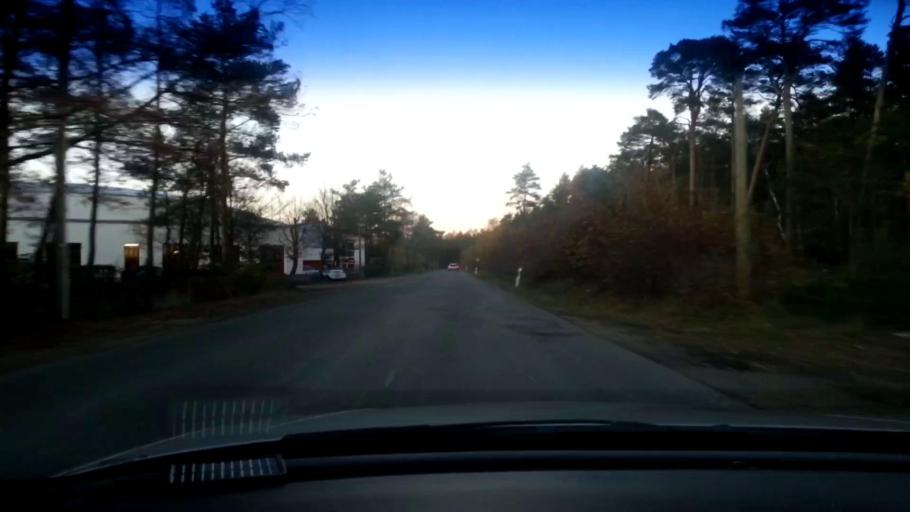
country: DE
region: Bavaria
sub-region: Upper Franconia
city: Bamberg
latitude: 49.8937
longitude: 10.9292
